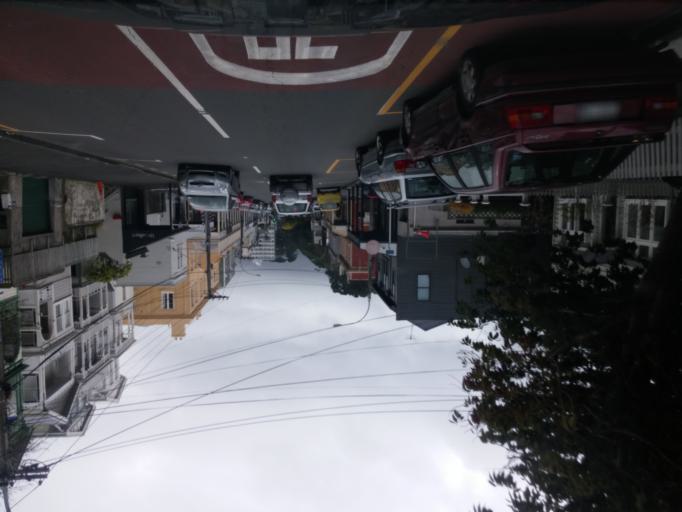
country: NZ
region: Wellington
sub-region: Wellington City
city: Kelburn
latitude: -41.2776
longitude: 174.7706
